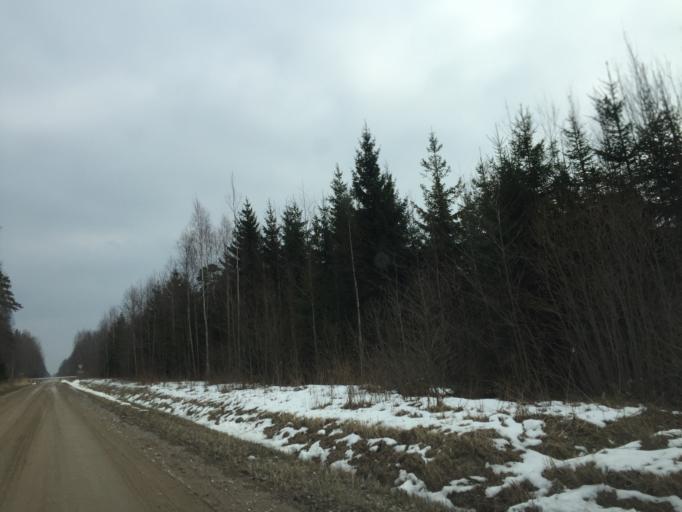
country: LV
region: Salacgrivas
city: Ainazi
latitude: 58.0310
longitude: 24.4993
